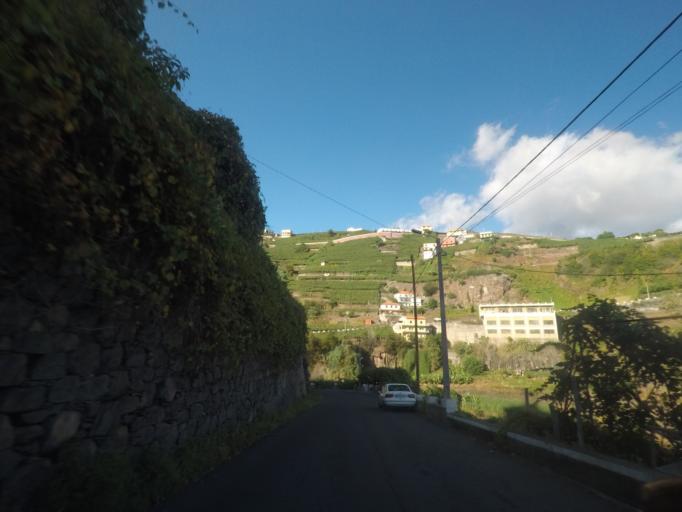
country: PT
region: Madeira
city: Camara de Lobos
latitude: 32.6706
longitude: -16.9864
